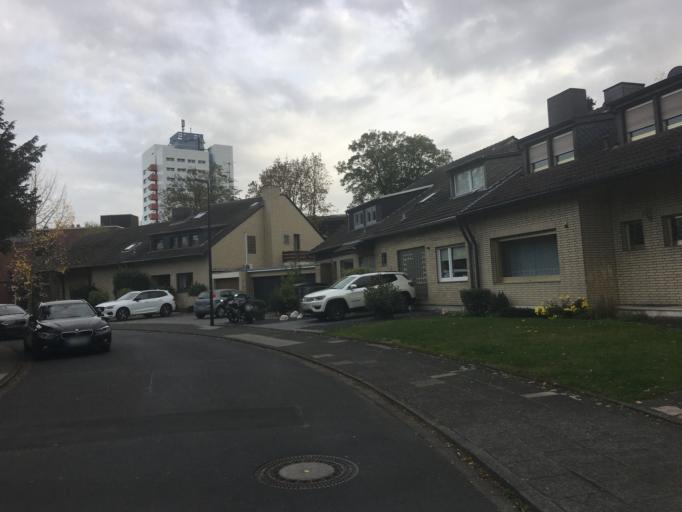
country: DE
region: North Rhine-Westphalia
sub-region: Regierungsbezirk Koln
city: Hurth
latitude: 50.8937
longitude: 6.9076
